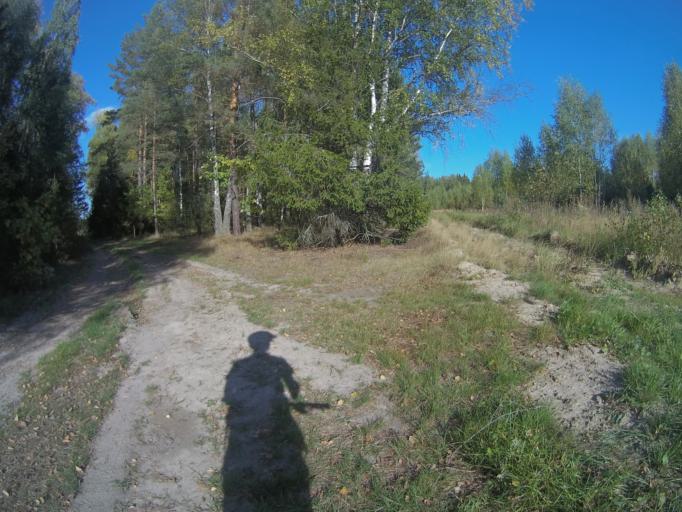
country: RU
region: Vladimir
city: Golovino
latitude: 55.9889
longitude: 40.4528
